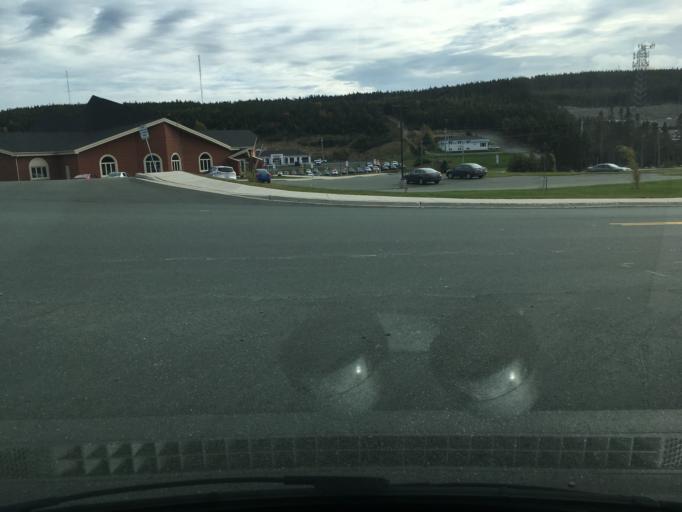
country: CA
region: Newfoundland and Labrador
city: Mount Pearl
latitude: 47.5492
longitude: -52.7859
